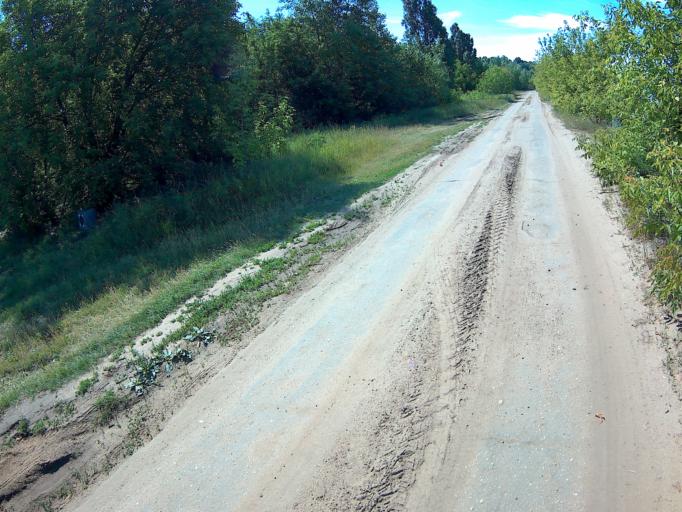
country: RU
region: Nizjnij Novgorod
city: Nizhniy Novgorod
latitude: 56.2584
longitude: 43.9655
